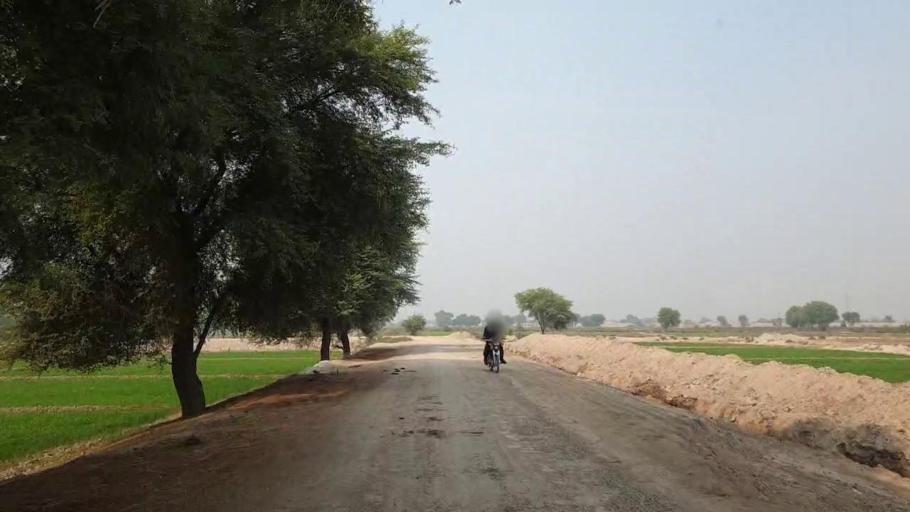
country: PK
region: Sindh
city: Bhan
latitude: 26.5302
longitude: 67.7139
